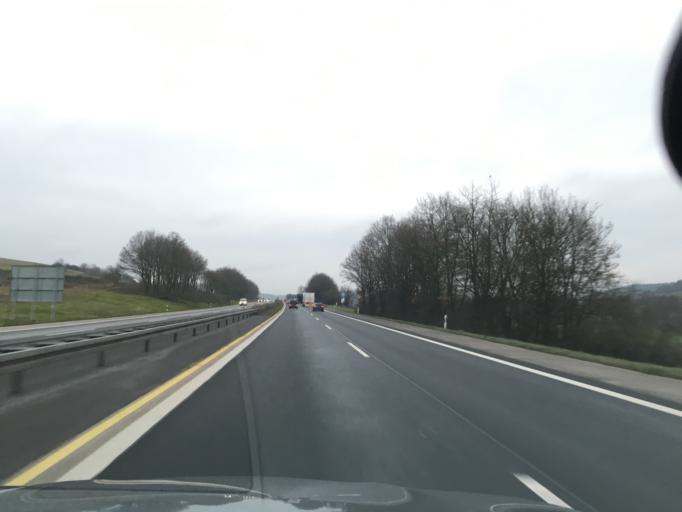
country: DE
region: Bavaria
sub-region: Regierungsbezirk Unterfranken
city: Geiselwind
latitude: 49.7691
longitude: 10.4880
